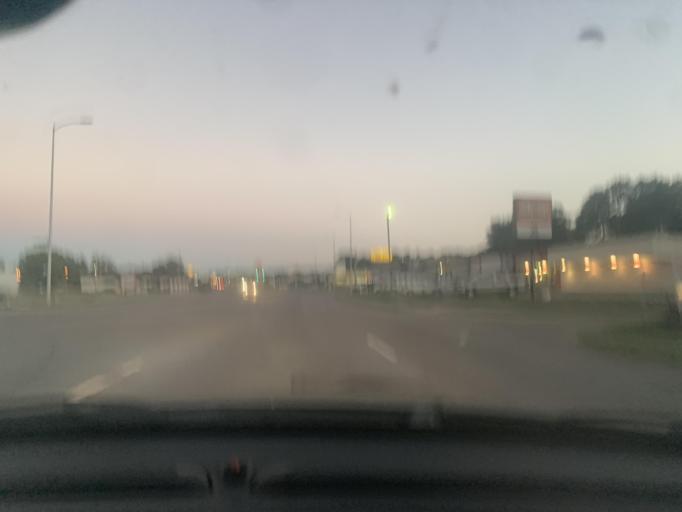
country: US
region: Nebraska
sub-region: Douglas County
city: Ralston
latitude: 41.2938
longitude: -96.0528
